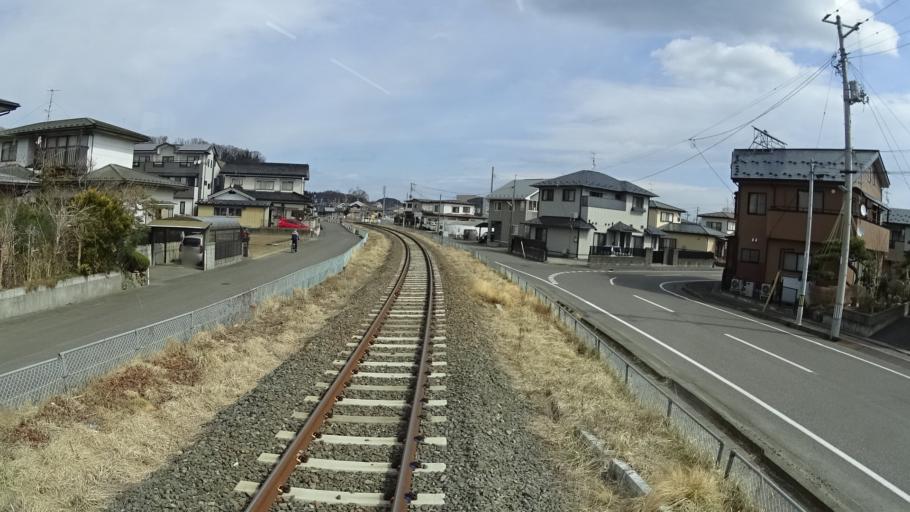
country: JP
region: Iwate
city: Miyako
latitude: 39.6278
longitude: 141.9603
